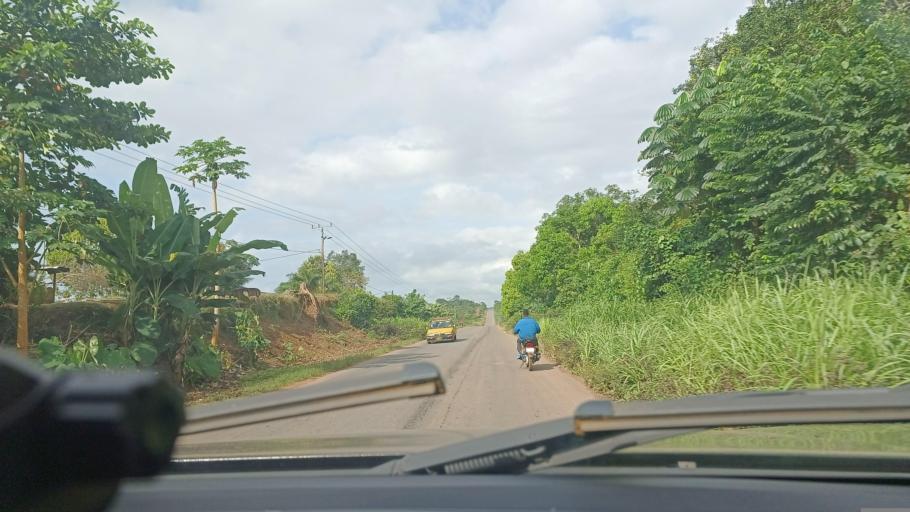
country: LR
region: Bomi
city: Tubmanburg
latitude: 6.7319
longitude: -10.9974
